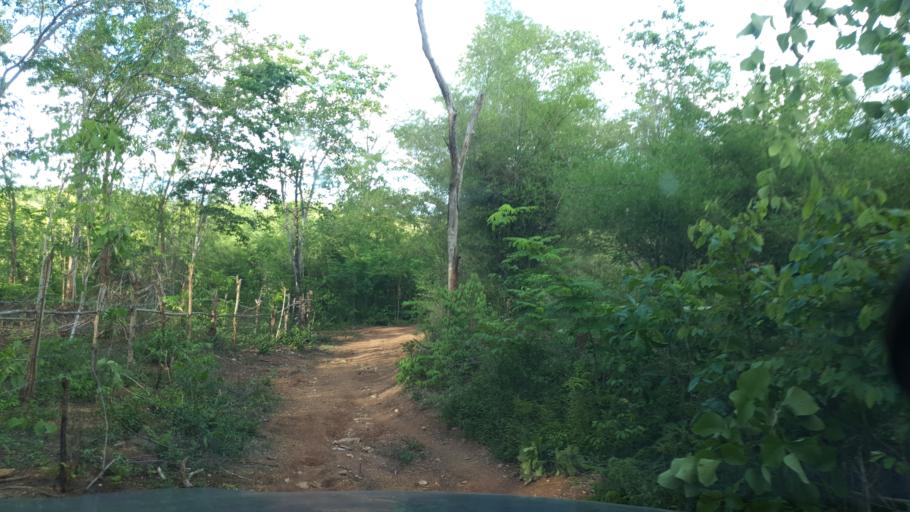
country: TH
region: Lampang
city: Sop Prap
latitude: 17.8916
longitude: 99.2855
